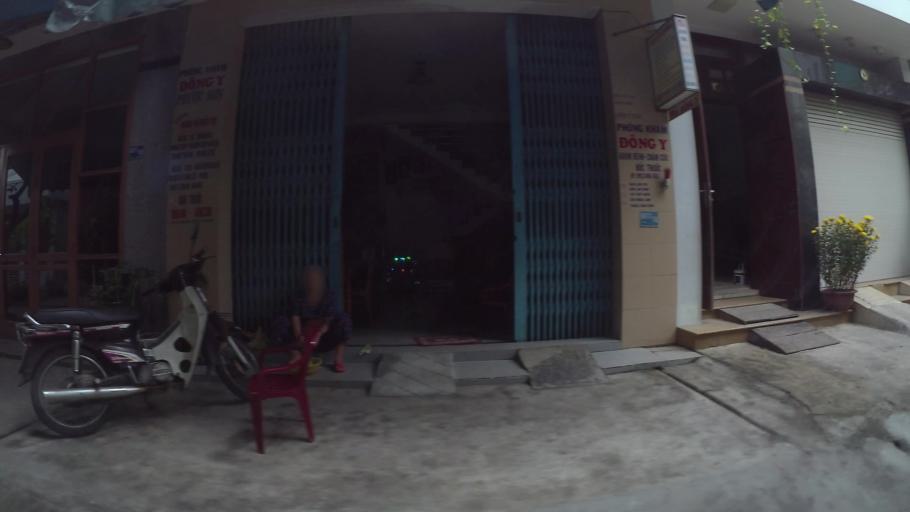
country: VN
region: Da Nang
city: Thanh Khe
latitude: 16.0712
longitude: 108.1864
